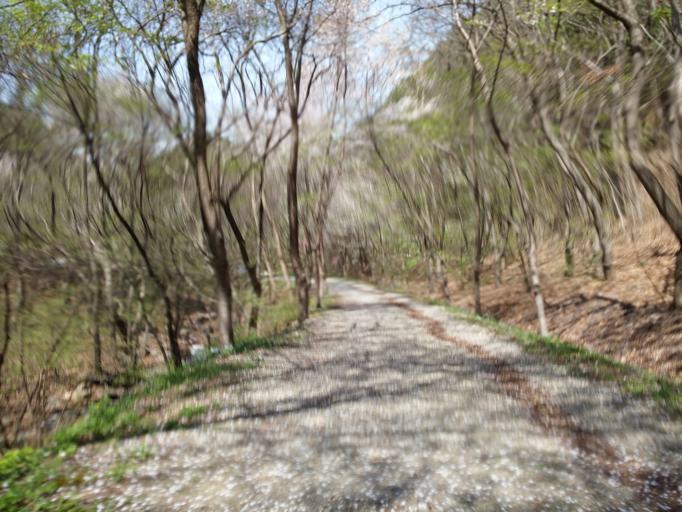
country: KR
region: Daejeon
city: Daejeon
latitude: 36.2770
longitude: 127.4813
